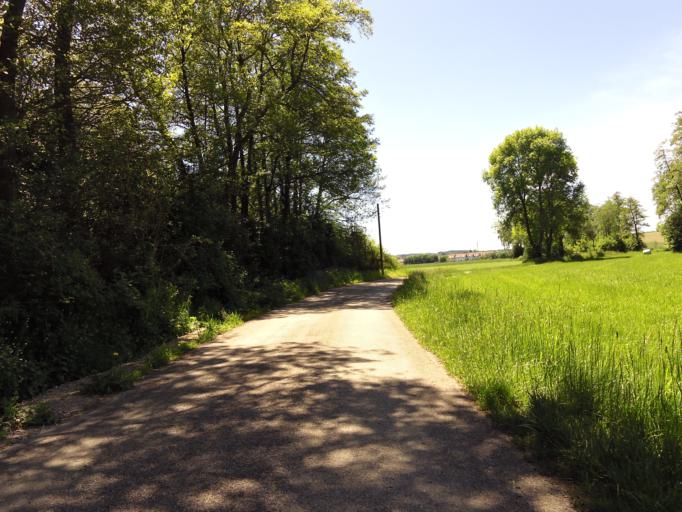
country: DE
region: Bavaria
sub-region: Upper Bavaria
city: Langenbach
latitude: 48.4509
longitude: 11.8585
